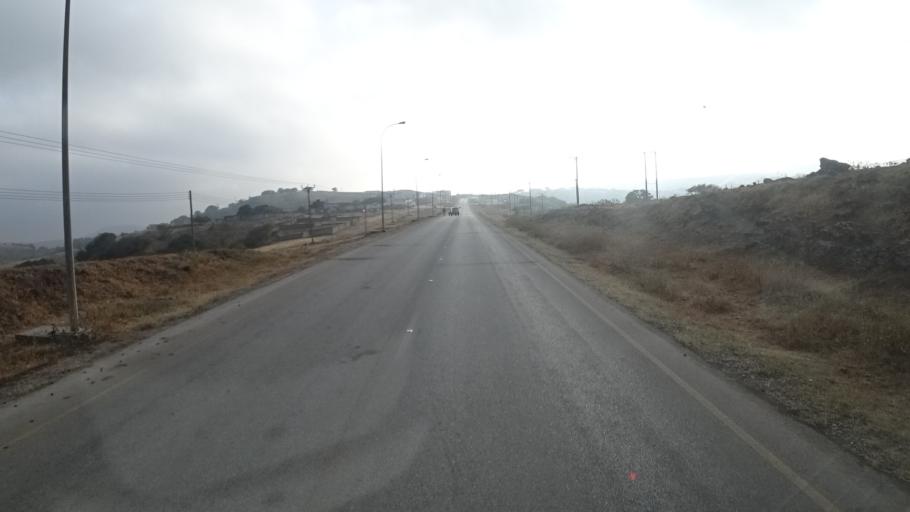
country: OM
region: Zufar
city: Salalah
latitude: 17.1230
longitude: 53.9932
